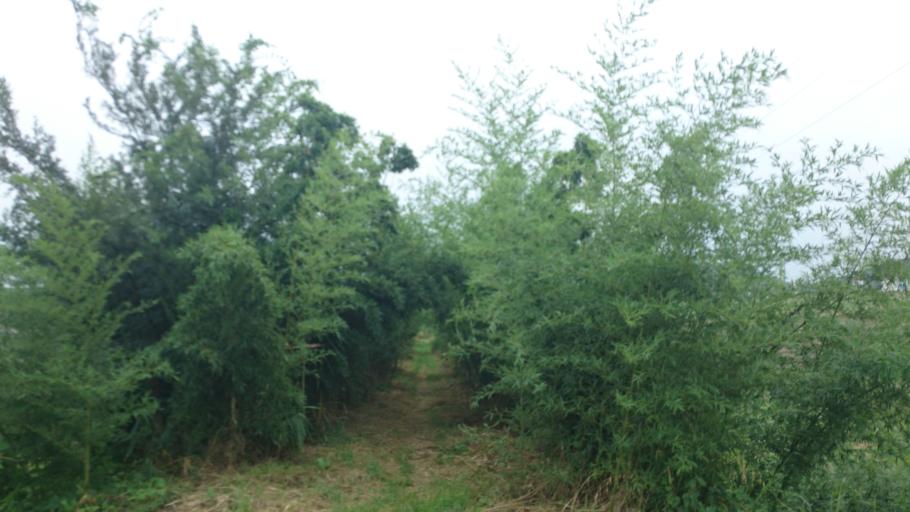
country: KR
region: Daegu
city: Hwawon
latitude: 35.8532
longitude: 128.4702
